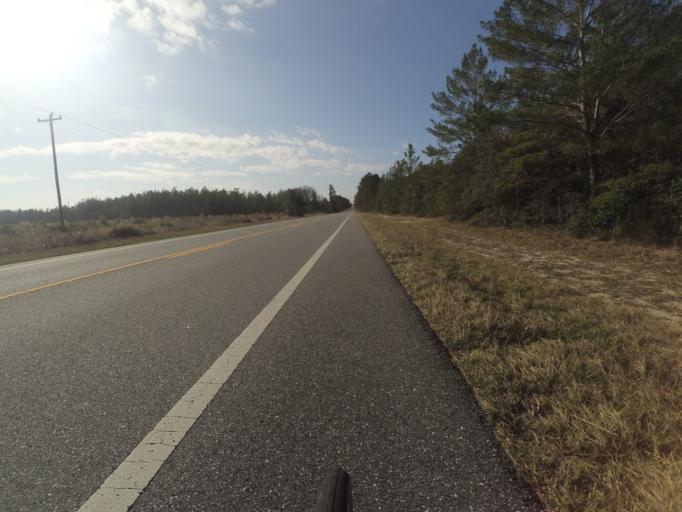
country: US
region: Florida
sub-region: Lake County
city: Astor
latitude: 29.0992
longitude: -81.6206
